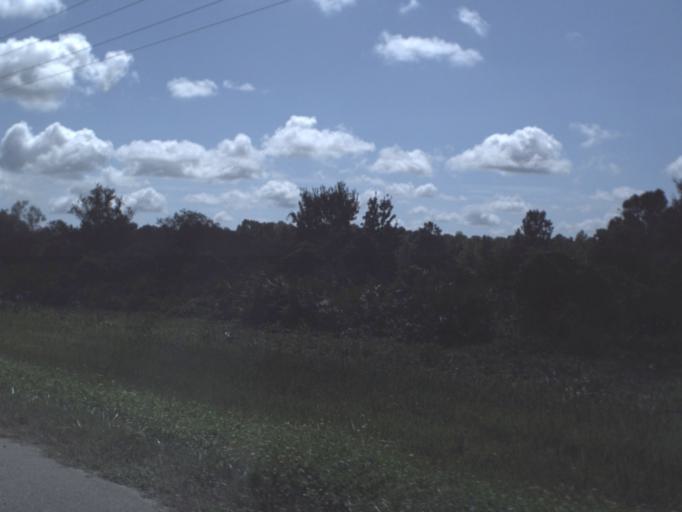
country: US
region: Florida
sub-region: Hillsborough County
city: Wimauma
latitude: 27.4599
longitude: -82.1784
